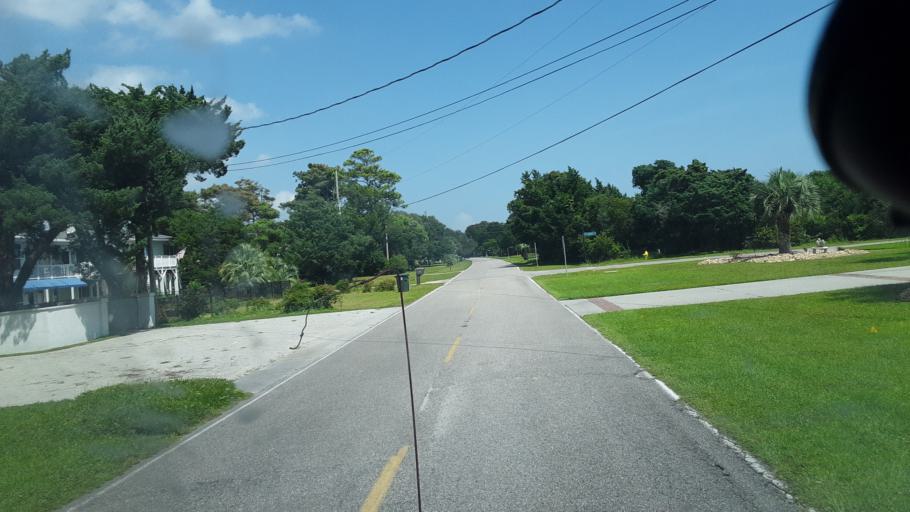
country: US
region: South Carolina
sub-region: Horry County
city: North Myrtle Beach
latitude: 33.8249
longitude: -78.6597
